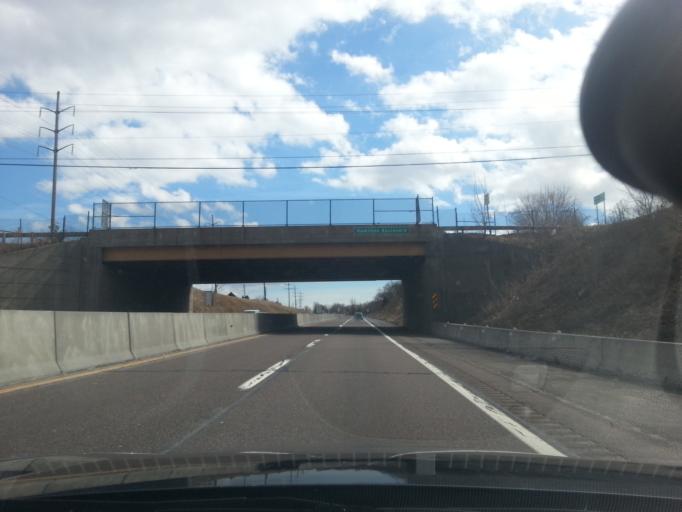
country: US
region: Pennsylvania
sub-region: Lehigh County
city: Wescosville
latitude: 40.5678
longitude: -75.5519
